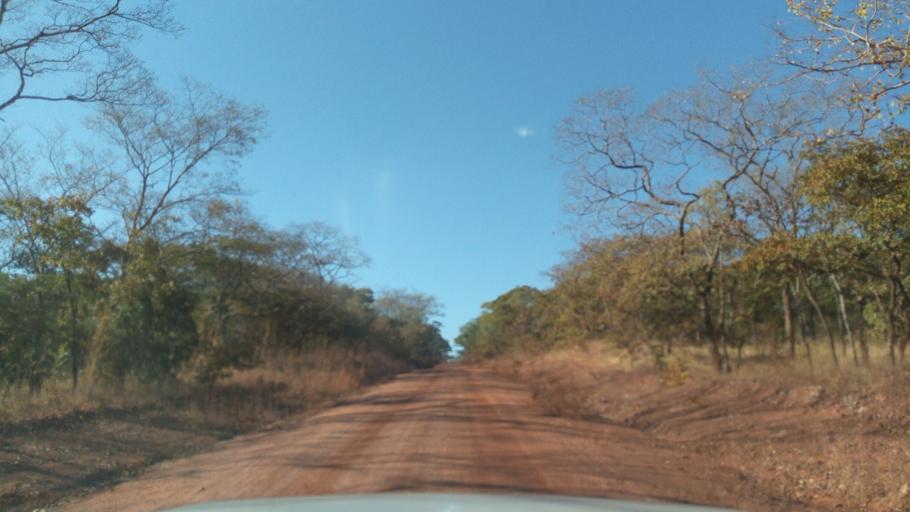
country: ZM
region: Luapula
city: Mwense
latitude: -10.5838
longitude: 28.4365
